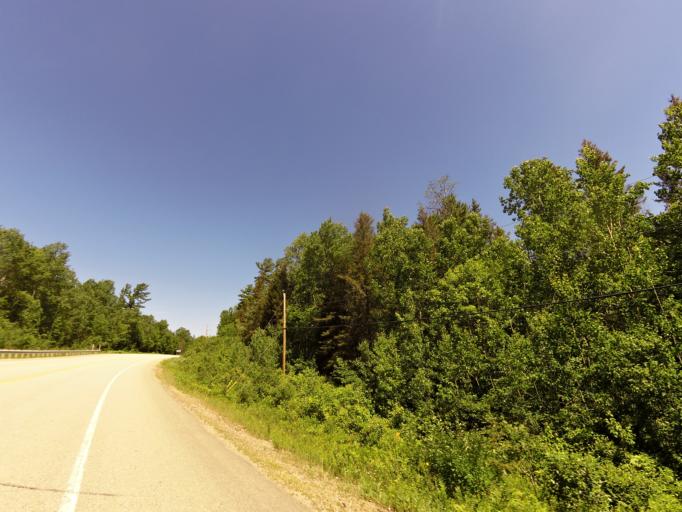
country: CA
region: Quebec
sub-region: Abitibi-Temiscamingue
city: Temiscaming
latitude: 46.7508
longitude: -79.0768
